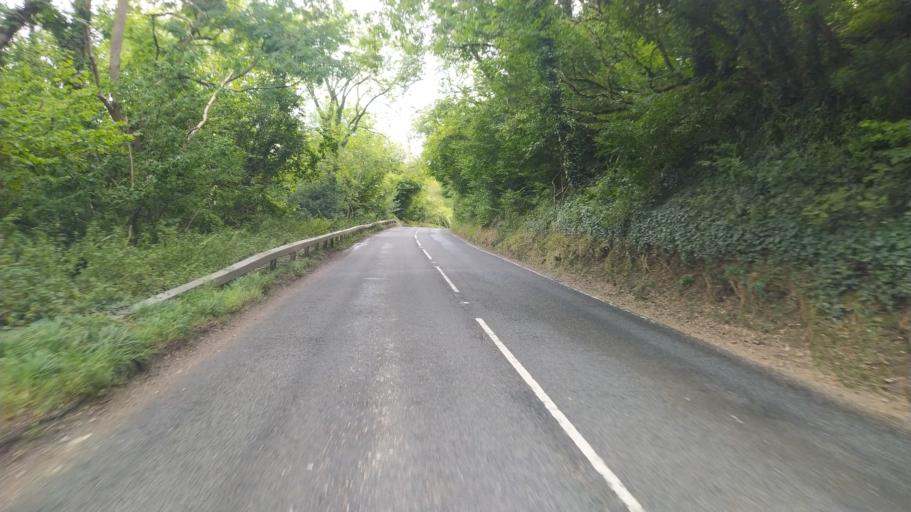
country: GB
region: England
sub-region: Dorset
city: Blandford Forum
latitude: 50.8824
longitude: -2.2094
